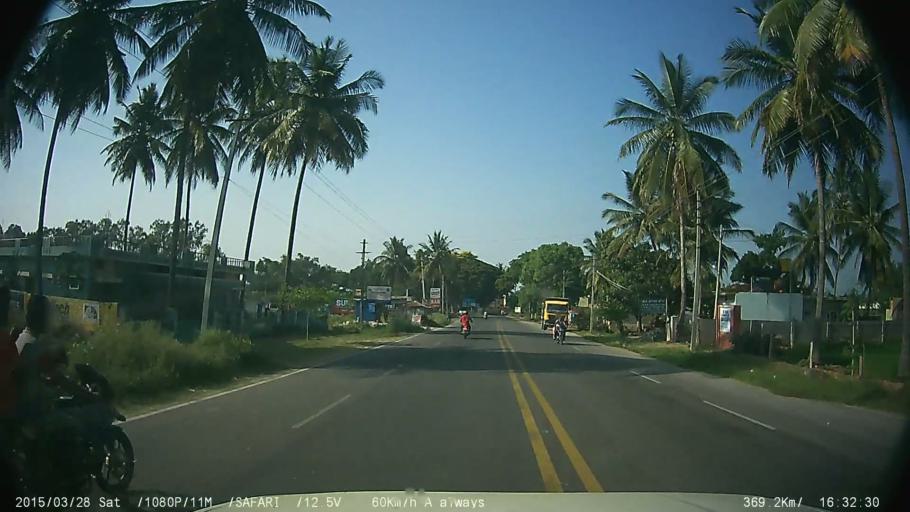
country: IN
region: Karnataka
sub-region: Mandya
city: Shrirangapattana
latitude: 12.3901
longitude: 76.6273
